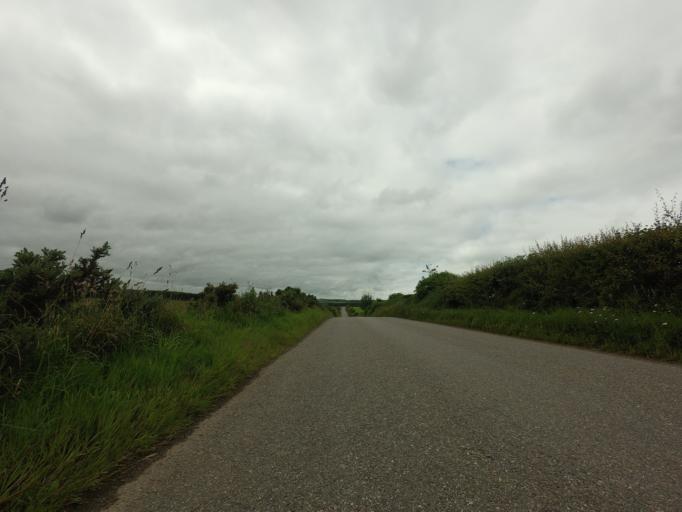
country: GB
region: Scotland
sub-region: Aberdeenshire
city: Mintlaw
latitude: 57.5250
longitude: -2.1401
